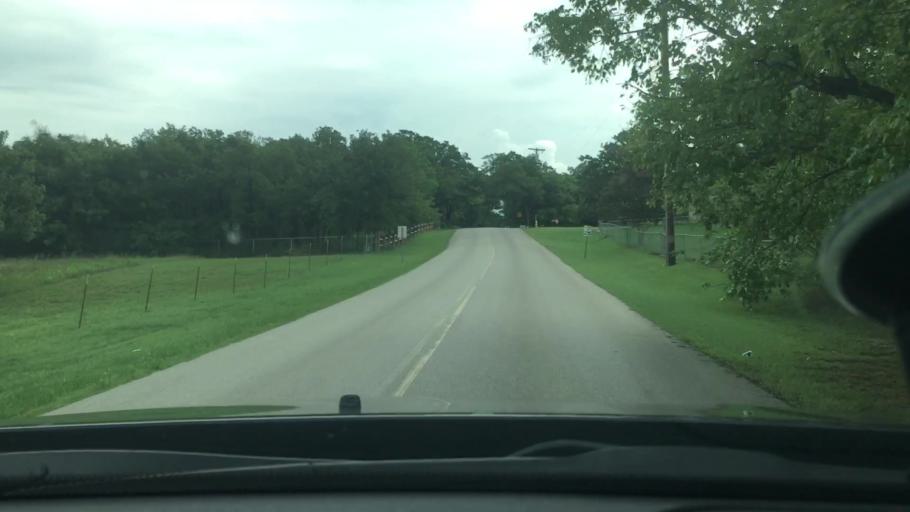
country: US
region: Oklahoma
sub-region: Carter County
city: Healdton
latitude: 34.2164
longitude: -97.4819
